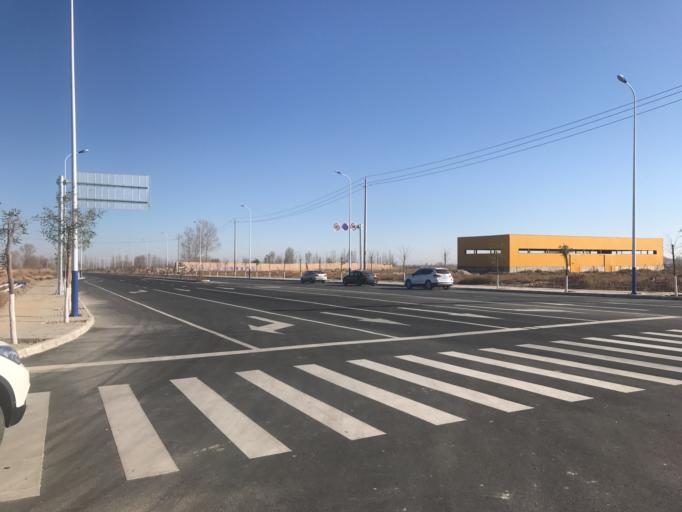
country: CN
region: Gansu Sheng
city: Gulang
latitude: 37.6892
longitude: 102.8565
